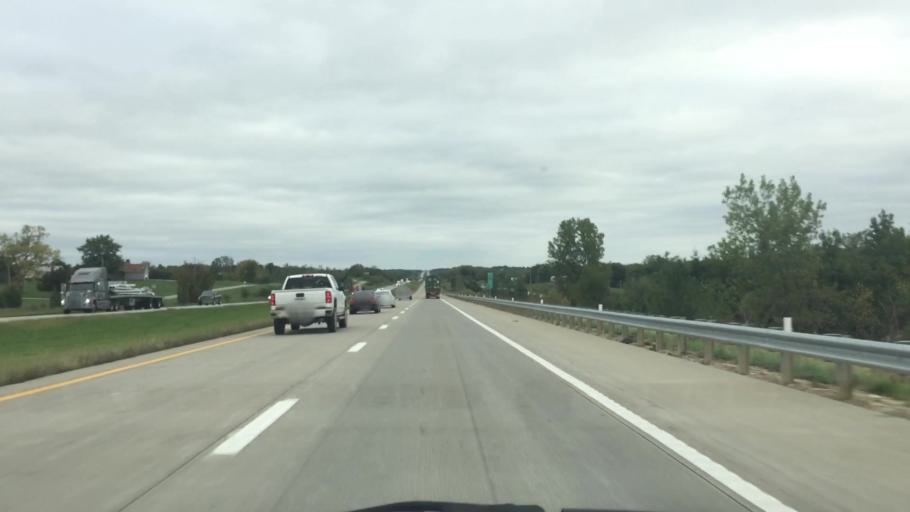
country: US
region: Missouri
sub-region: Clinton County
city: Cameron
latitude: 39.6526
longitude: -94.2394
